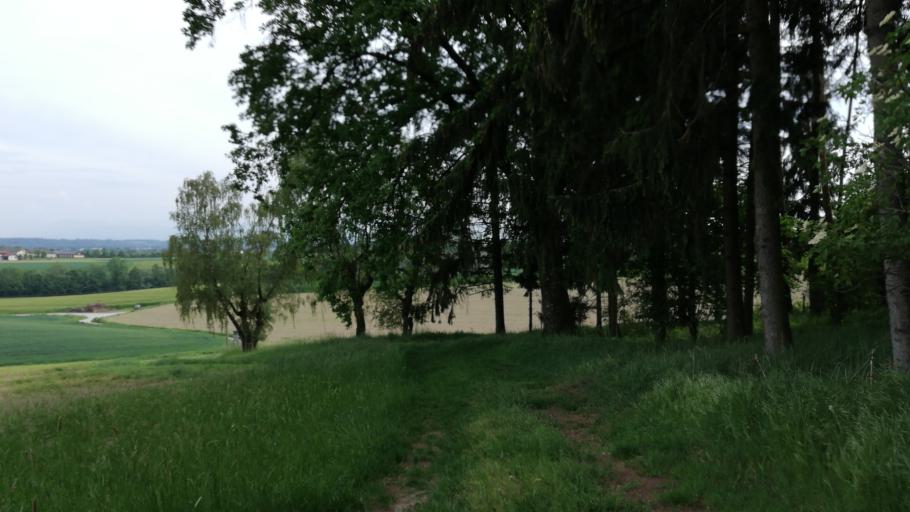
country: AT
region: Upper Austria
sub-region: Wels-Land
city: Gunskirchen
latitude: 48.1701
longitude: 13.9425
